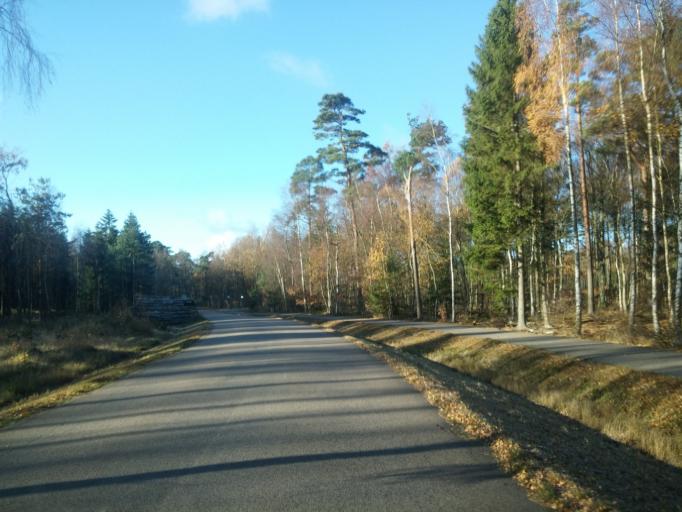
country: SE
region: Skane
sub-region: Angelholms Kommun
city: AEngelholm
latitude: 56.2339
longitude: 12.8296
